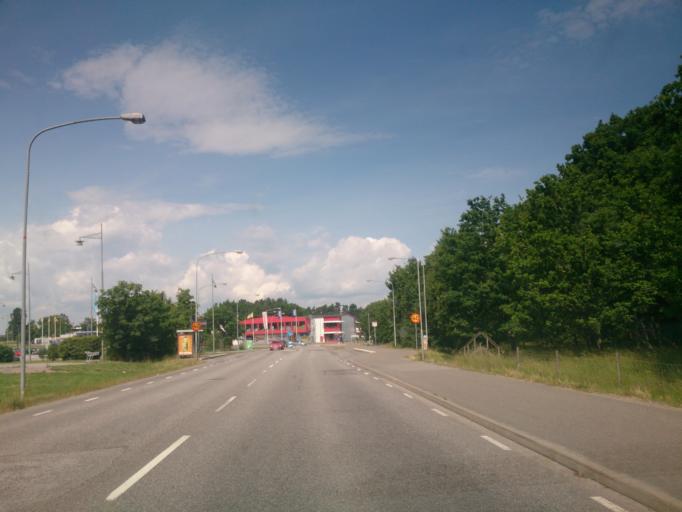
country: SE
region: OEstergoetland
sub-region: Norrkopings Kommun
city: Norrkoping
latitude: 58.6157
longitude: 16.1646
